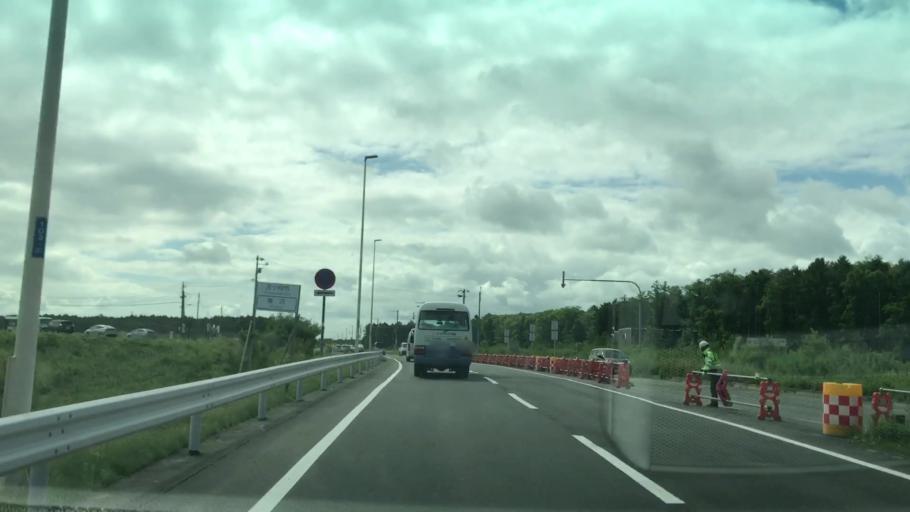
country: JP
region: Hokkaido
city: Chitose
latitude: 42.7732
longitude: 141.6790
